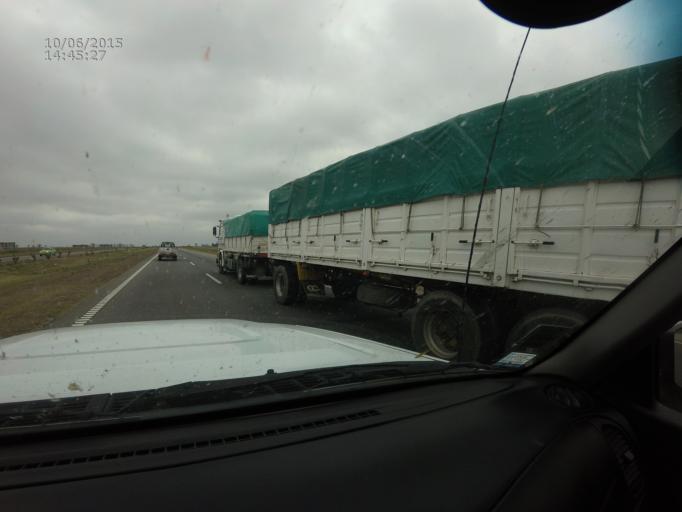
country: AR
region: Cordoba
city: Oliva
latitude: -31.9872
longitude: -63.5658
